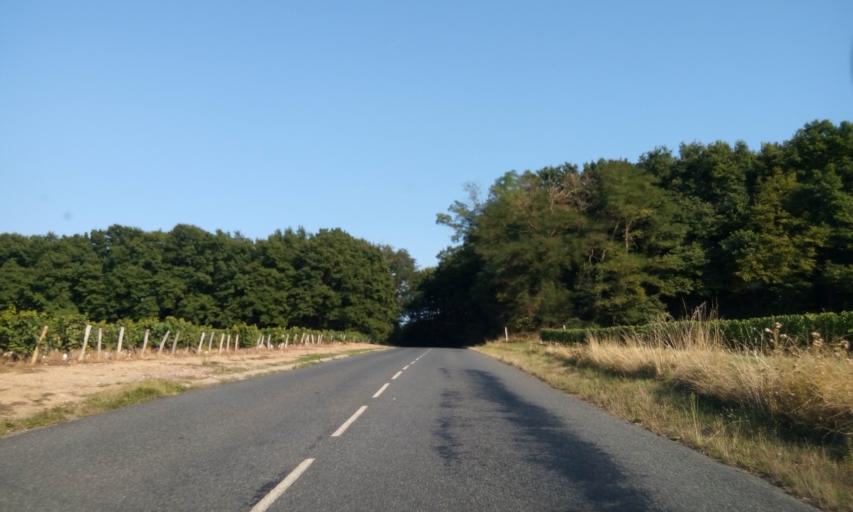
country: FR
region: Rhone-Alpes
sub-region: Departement du Rhone
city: Charnay
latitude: 45.9266
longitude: 4.6641
